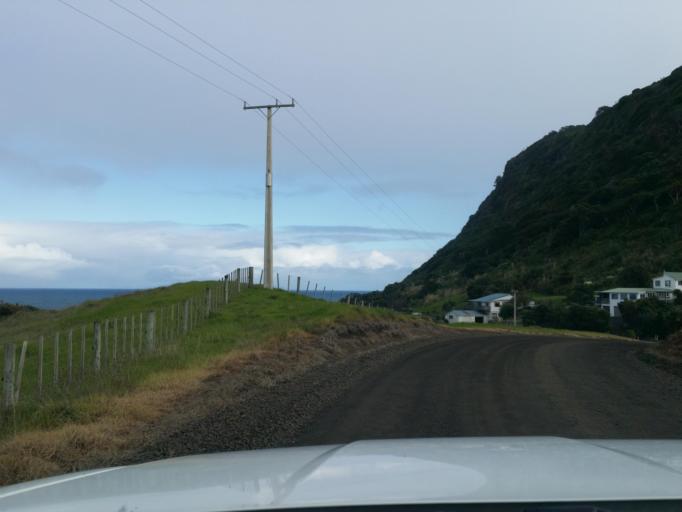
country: NZ
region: Northland
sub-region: Kaipara District
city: Dargaville
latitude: -35.7689
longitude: 173.5796
